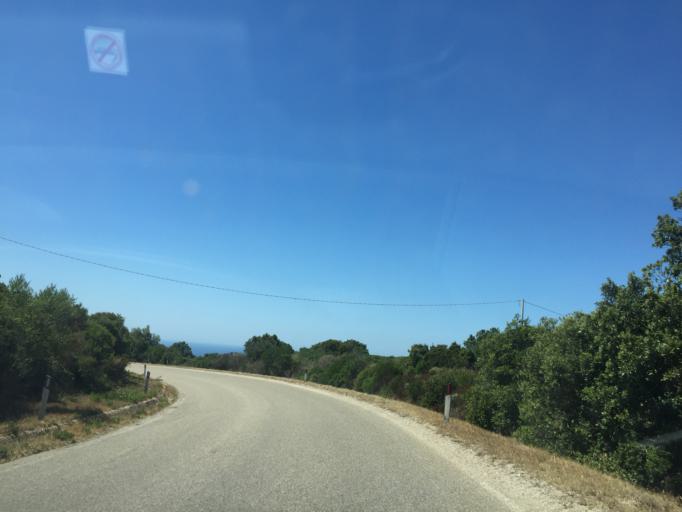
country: IT
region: Sardinia
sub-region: Provincia di Olbia-Tempio
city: Aglientu
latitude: 41.0890
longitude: 9.1181
